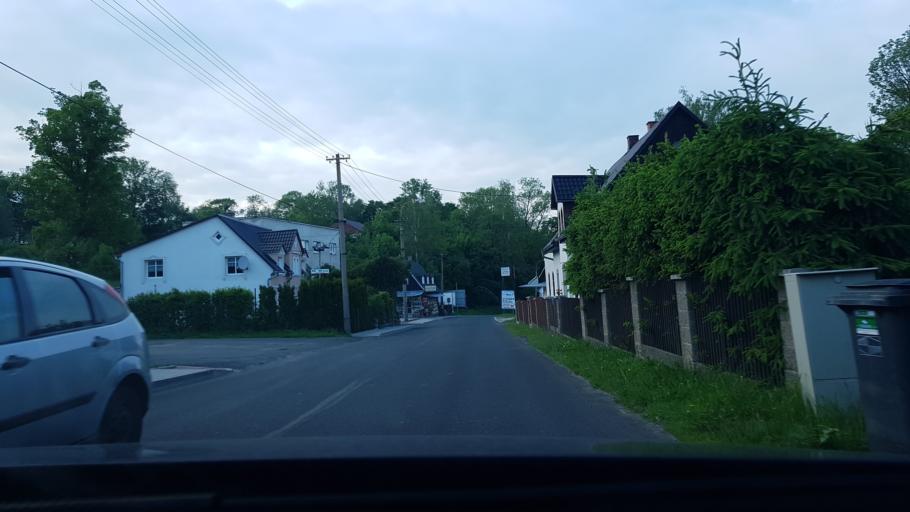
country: CZ
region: Ustecky
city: Libouchec
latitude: 50.8061
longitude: 13.9796
